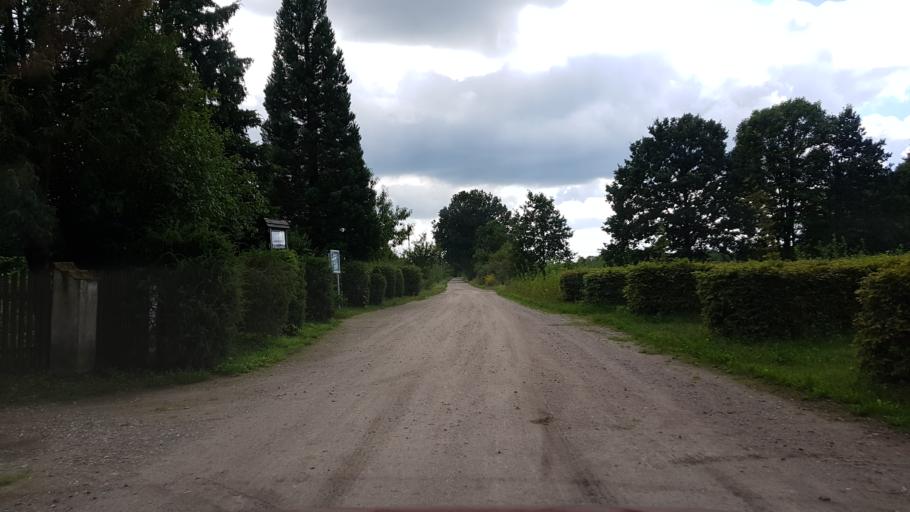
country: PL
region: West Pomeranian Voivodeship
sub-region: Powiat bialogardzki
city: Tychowo
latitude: 53.9990
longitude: 16.3045
